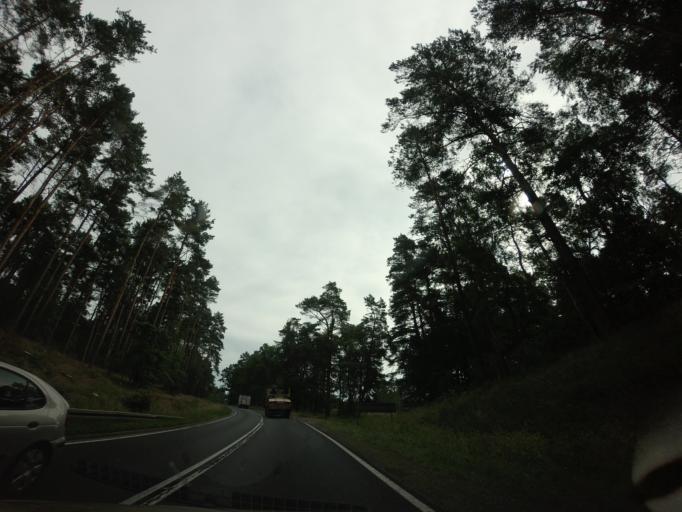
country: PL
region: West Pomeranian Voivodeship
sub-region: Powiat drawski
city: Kalisz Pomorski
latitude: 53.2916
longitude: 15.9538
